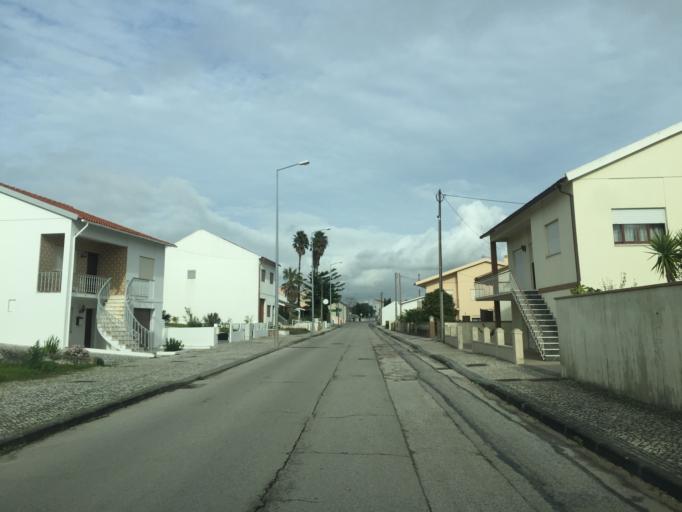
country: PT
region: Coimbra
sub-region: Figueira da Foz
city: Lavos
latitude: 40.0658
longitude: -8.8094
